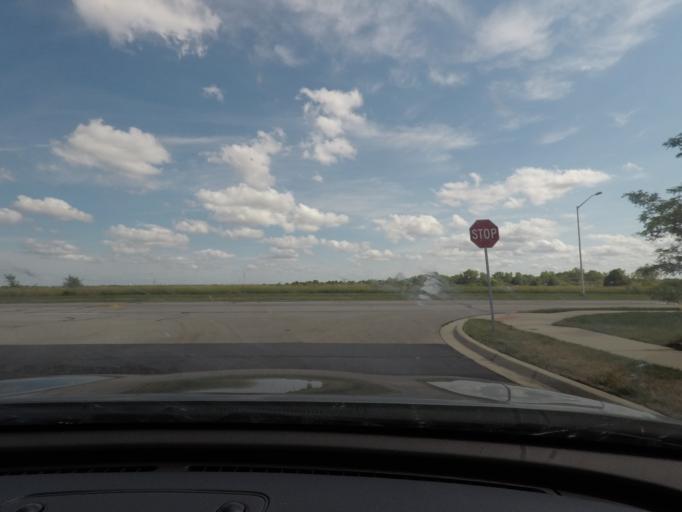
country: US
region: Kansas
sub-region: Johnson County
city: Olathe
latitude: 38.9453
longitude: -94.8186
